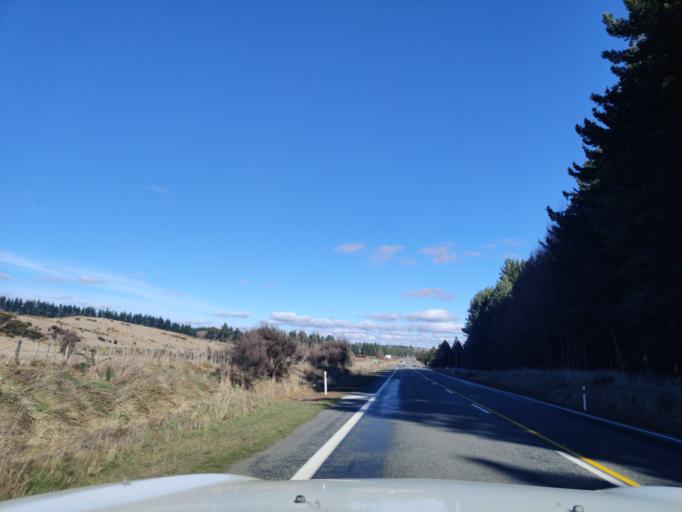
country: NZ
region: Manawatu-Wanganui
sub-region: Ruapehu District
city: Waiouru
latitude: -39.4520
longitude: 175.6777
